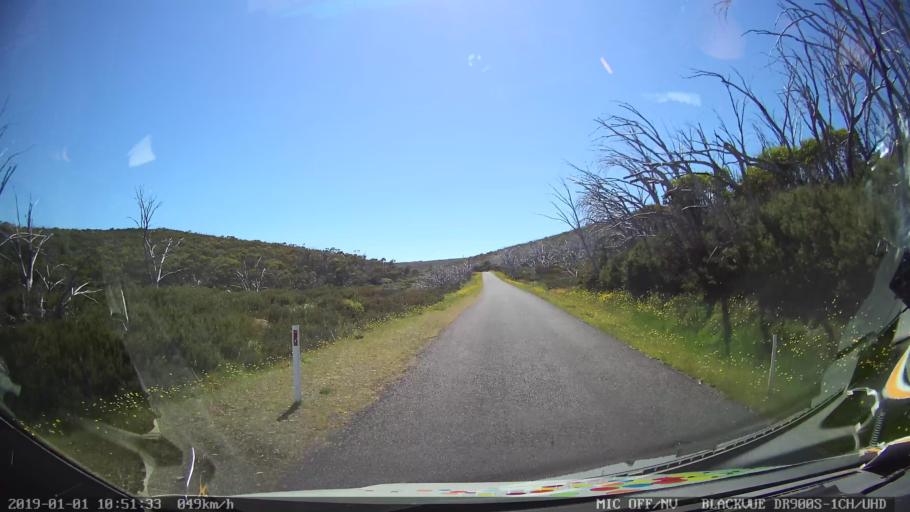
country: AU
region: New South Wales
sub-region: Snowy River
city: Jindabyne
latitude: -36.0202
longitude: 148.3715
